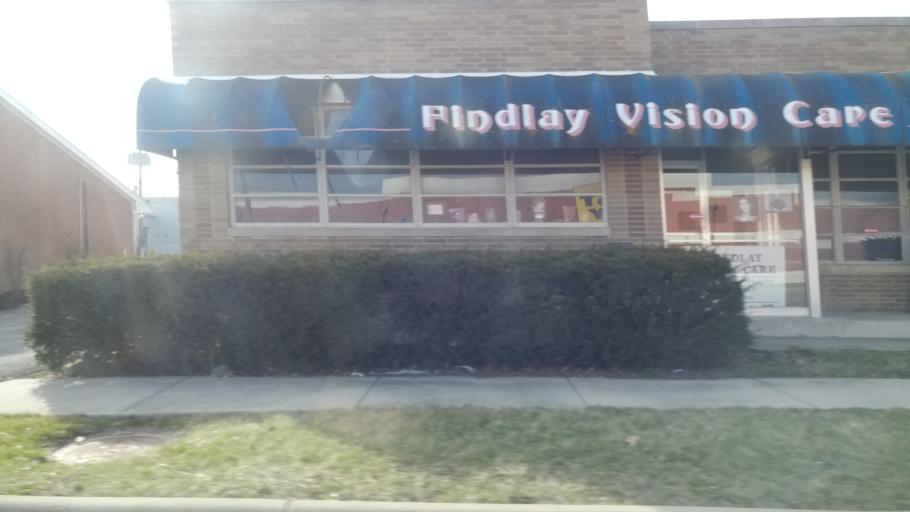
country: US
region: Ohio
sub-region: Hancock County
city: Findlay
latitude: 41.0542
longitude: -83.6162
